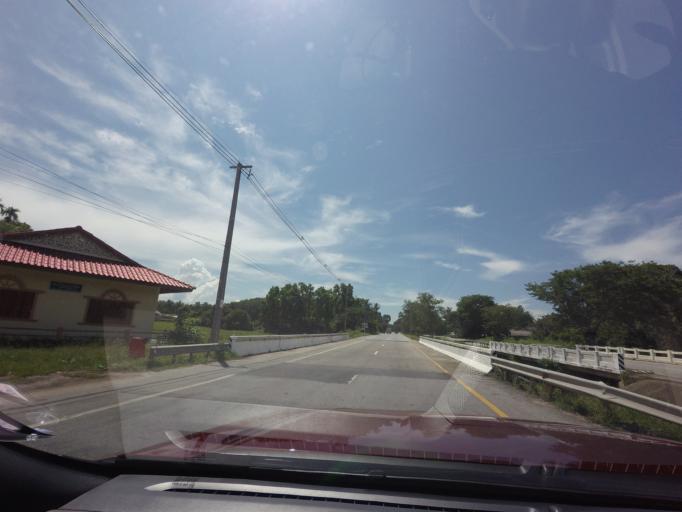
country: TH
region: Pattani
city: Sai Buri
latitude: 6.6587
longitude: 101.6255
